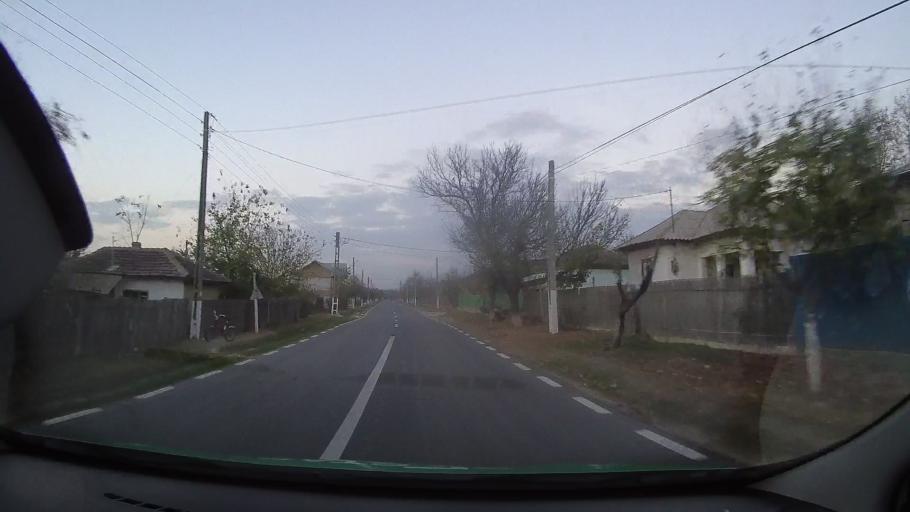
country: RO
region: Constanta
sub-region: Comuna Oltina
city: Oltina
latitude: 44.1660
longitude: 27.6668
